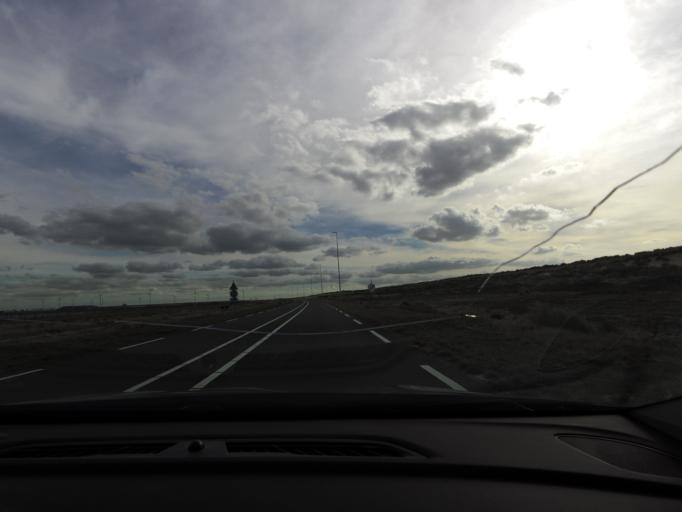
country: NL
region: South Holland
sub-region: Gemeente Goeree-Overflakkee
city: Goedereede
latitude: 51.9561
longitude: 3.9655
